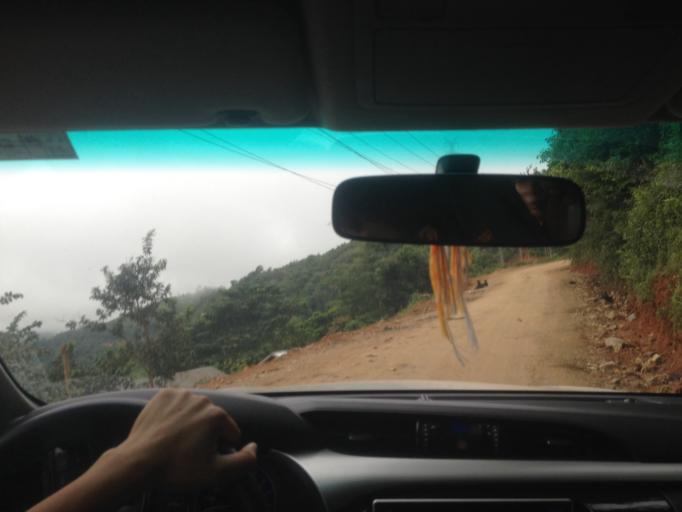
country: TH
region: Nan
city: Chaloem Phra Kiat
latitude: 19.9855
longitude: 101.1439
